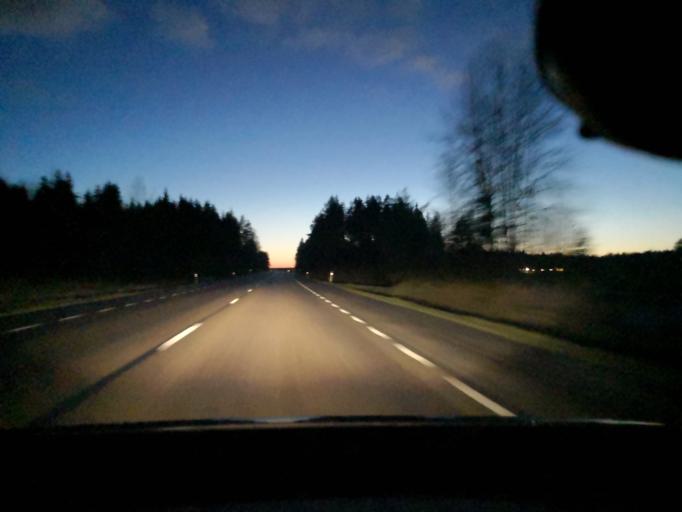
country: SE
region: Vaestmanland
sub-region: Sala Kommun
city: Sala
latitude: 59.9239
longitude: 16.6622
